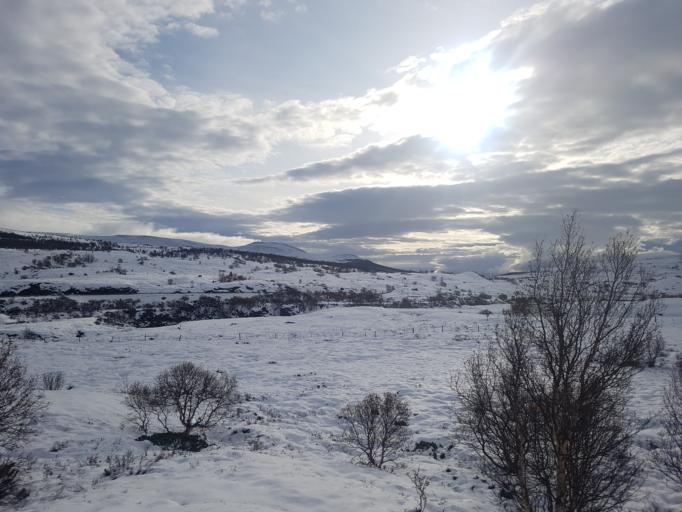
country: NO
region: Sor-Trondelag
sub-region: Oppdal
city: Oppdal
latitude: 62.2768
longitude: 9.5856
